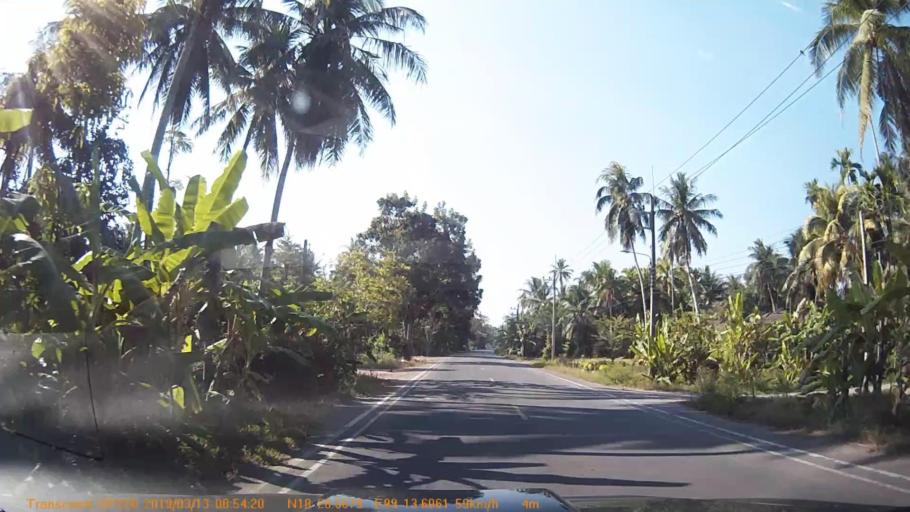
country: TH
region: Chumphon
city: Chumphon
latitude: 10.4759
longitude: 99.2268
